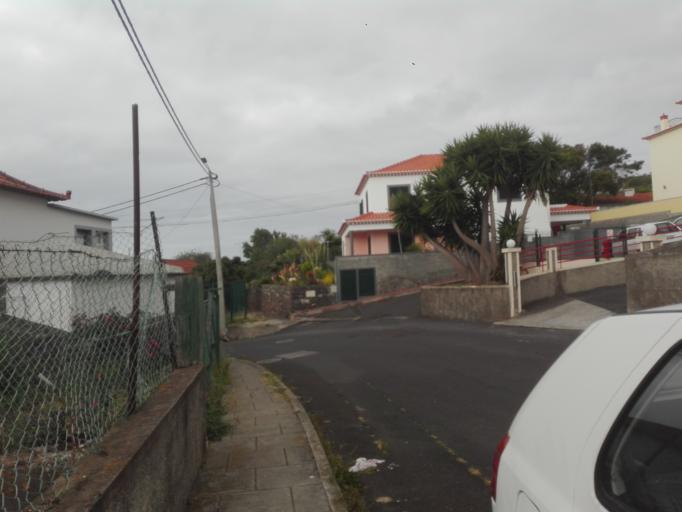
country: PT
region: Madeira
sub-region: Santa Cruz
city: Camacha
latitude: 32.6544
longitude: -16.8290
